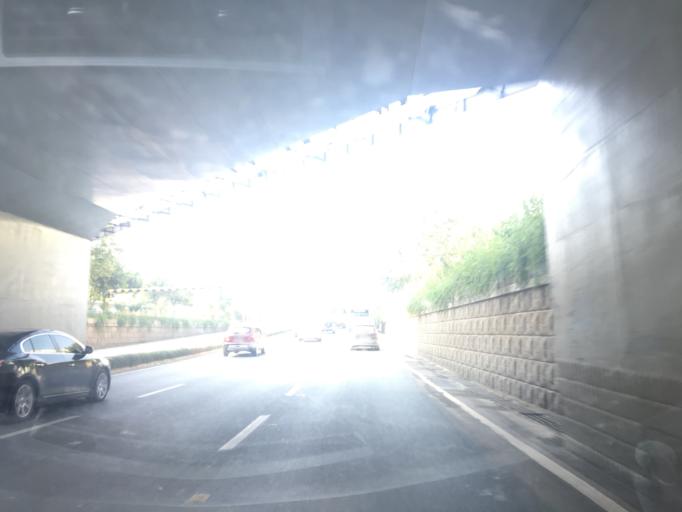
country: CN
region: Hubei
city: Jiang'an
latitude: 30.5695
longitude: 114.3133
